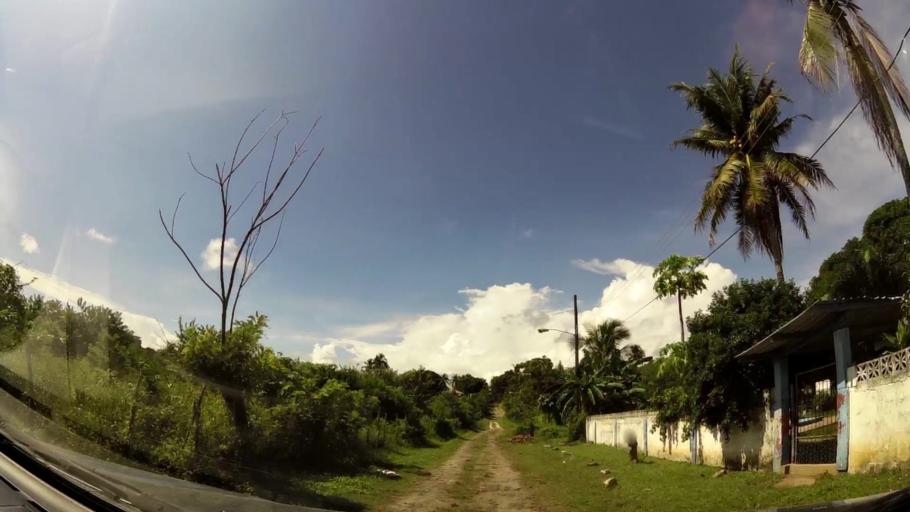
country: PA
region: Panama
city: Nueva Gorgona
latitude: 8.5551
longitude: -79.8645
